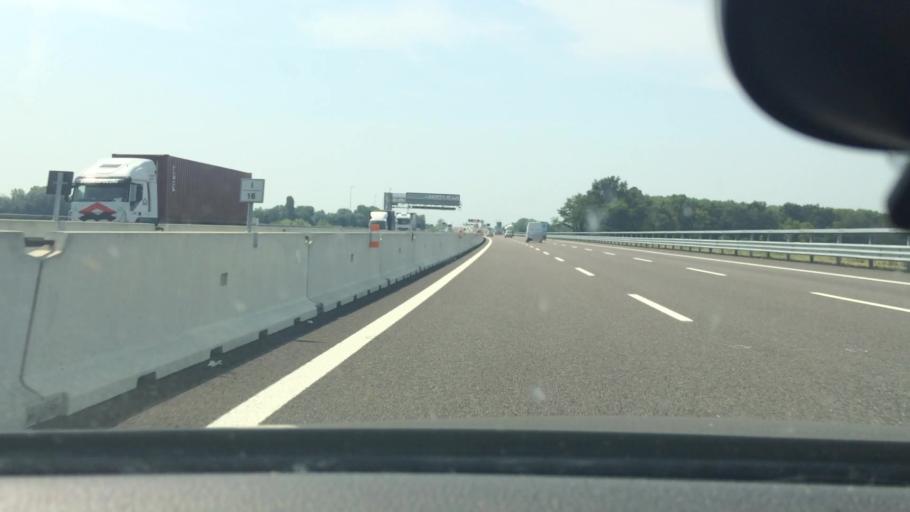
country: IT
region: Lombardy
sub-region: Provincia di Lodi
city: Merlino
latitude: 45.4502
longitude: 9.4290
